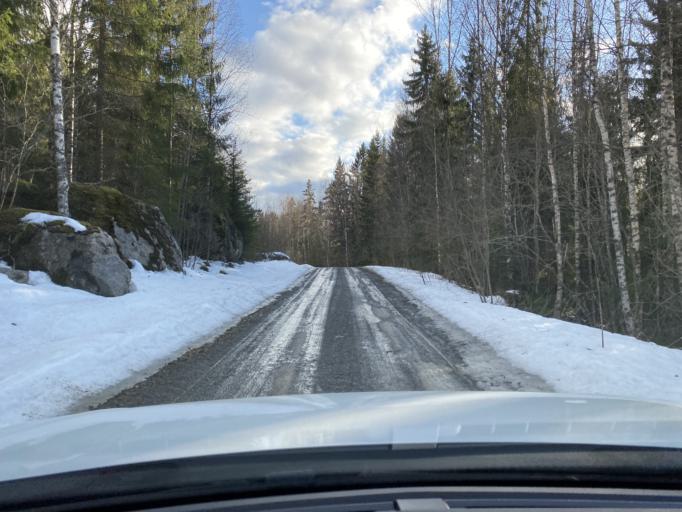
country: FI
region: Pirkanmaa
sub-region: Lounais-Pirkanmaa
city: Mouhijaervi
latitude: 61.4528
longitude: 22.9596
